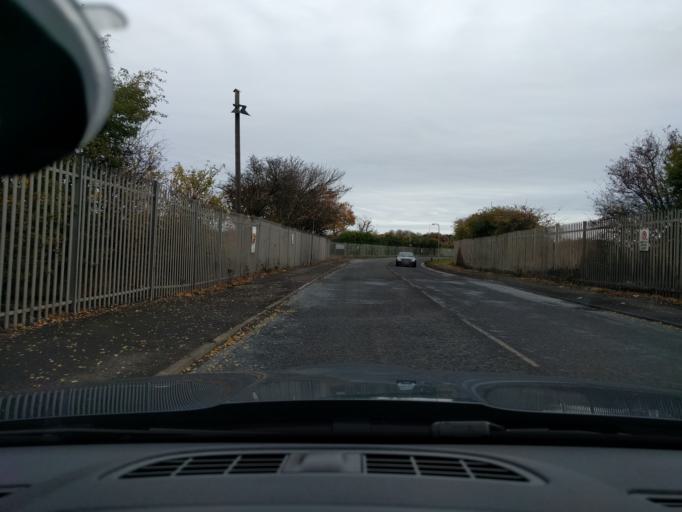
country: GB
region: England
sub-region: Northumberland
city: Blyth
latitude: 55.1441
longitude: -1.5287
